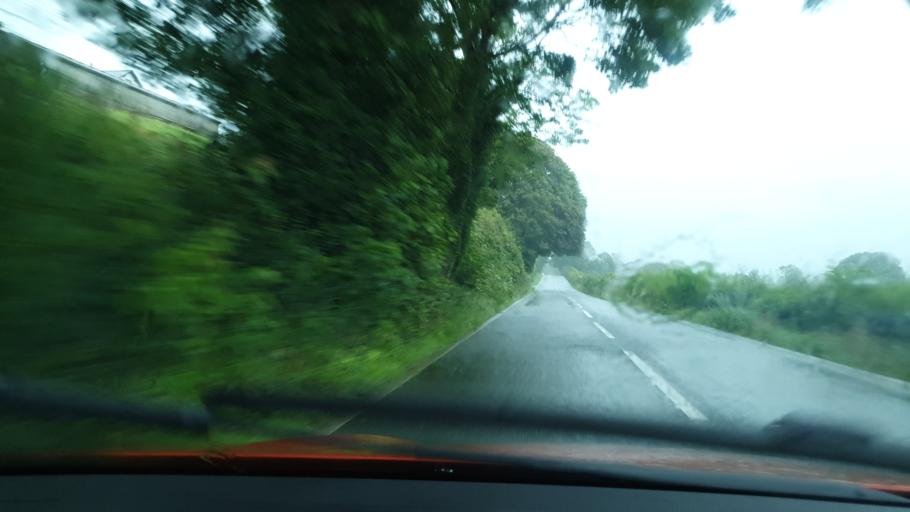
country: GB
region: England
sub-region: Cumbria
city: Askam in Furness
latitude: 54.2638
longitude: -3.2009
